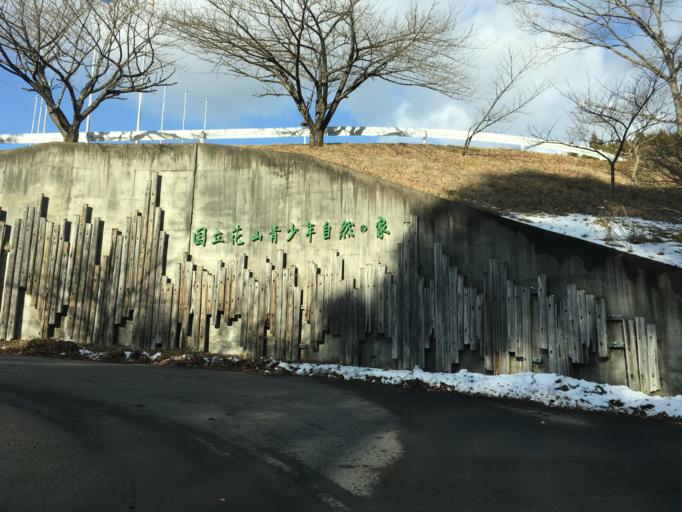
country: JP
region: Miyagi
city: Furukawa
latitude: 38.8221
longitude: 140.8335
